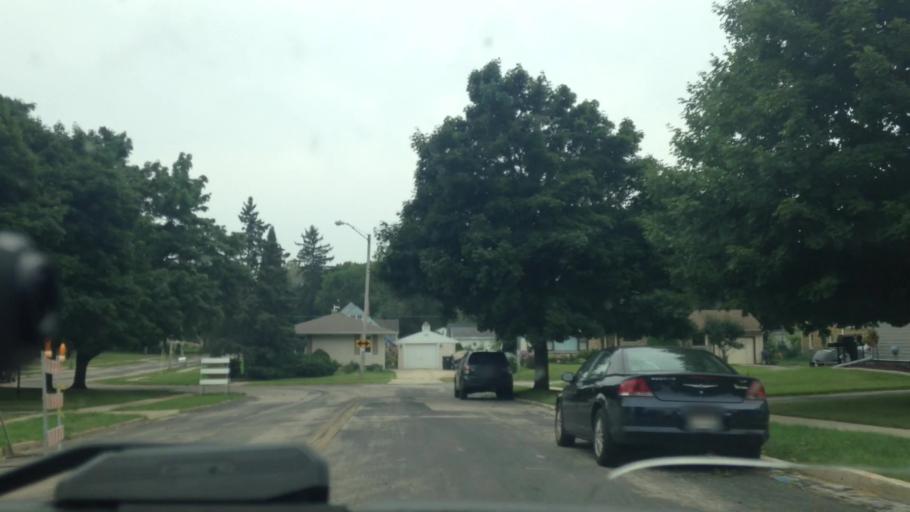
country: US
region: Wisconsin
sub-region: Waukesha County
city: Menomonee Falls
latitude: 43.1759
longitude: -88.1210
